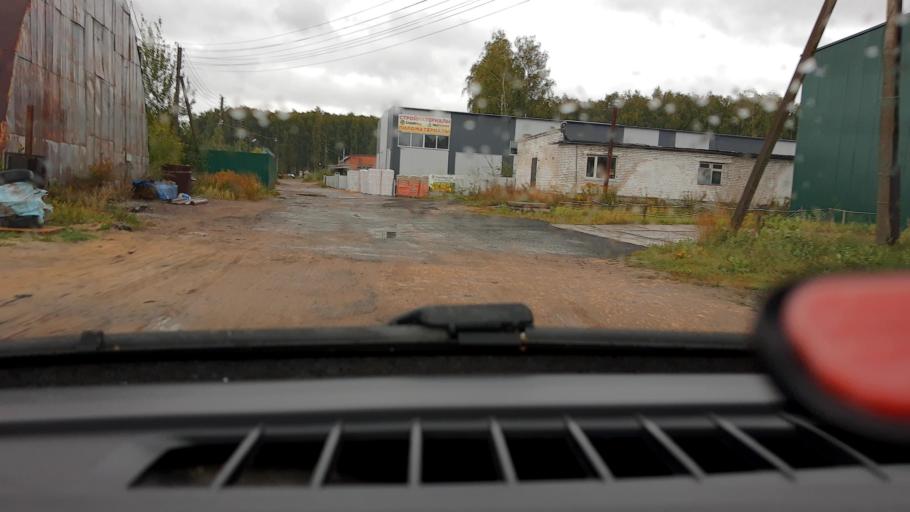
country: RU
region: Nizjnij Novgorod
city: Afonino
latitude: 56.1865
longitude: 44.1225
